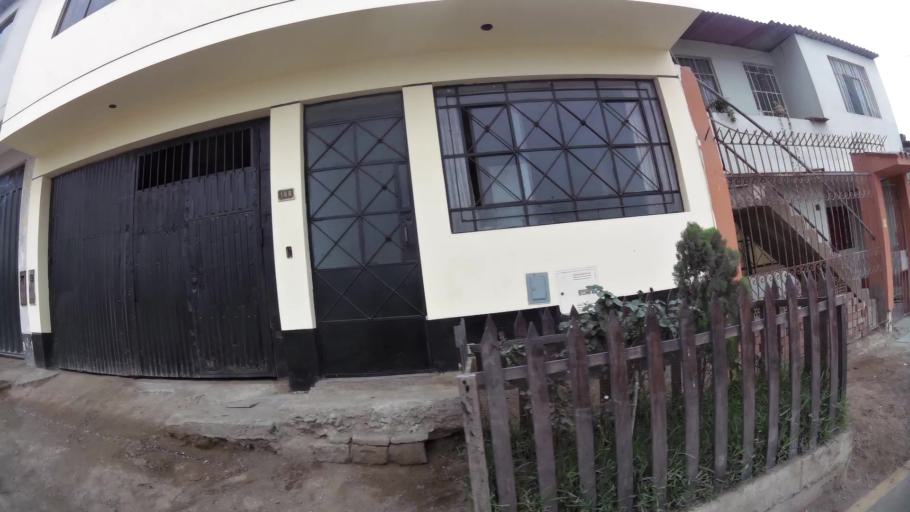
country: PE
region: Lima
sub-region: Lima
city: Surco
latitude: -12.1823
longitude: -76.9480
